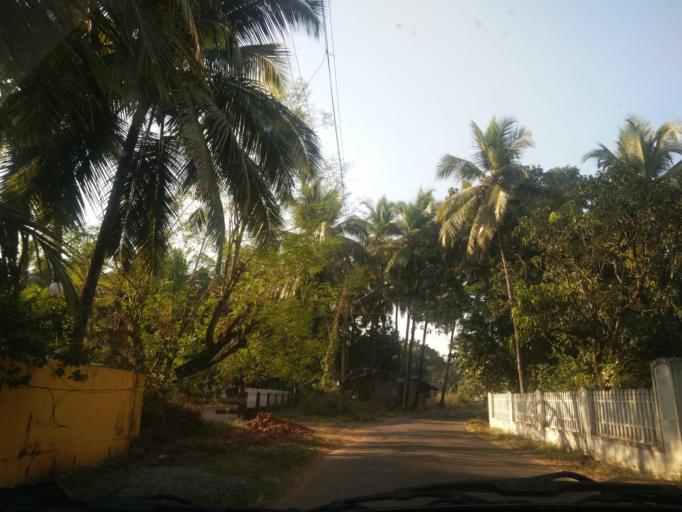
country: IN
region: Goa
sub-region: South Goa
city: Chinchinim
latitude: 15.2421
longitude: 73.9697
